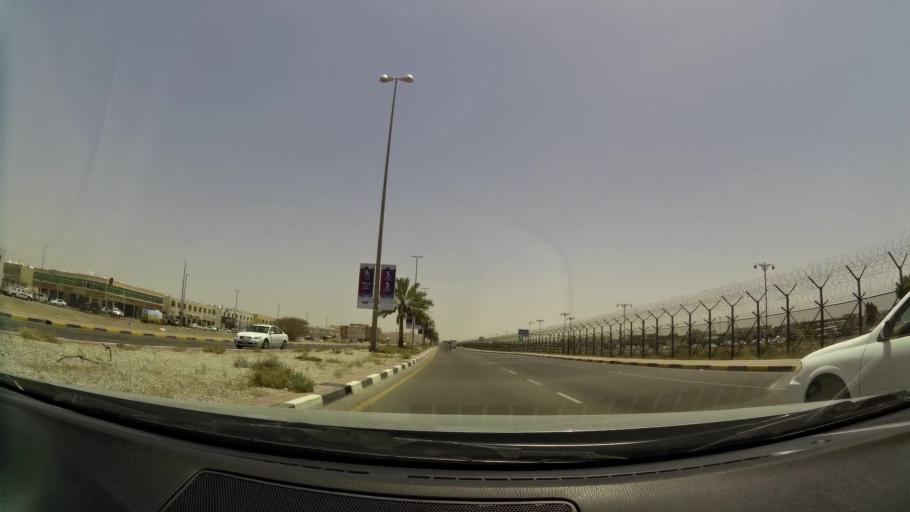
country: OM
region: Al Buraimi
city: Al Buraymi
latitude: 24.2635
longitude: 55.7694
